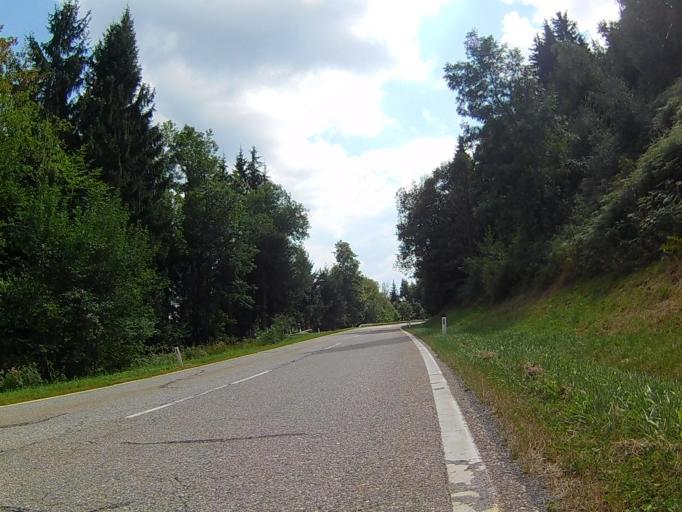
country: AT
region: Styria
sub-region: Politischer Bezirk Deutschlandsberg
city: Soboth
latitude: 46.6927
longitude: 15.1023
